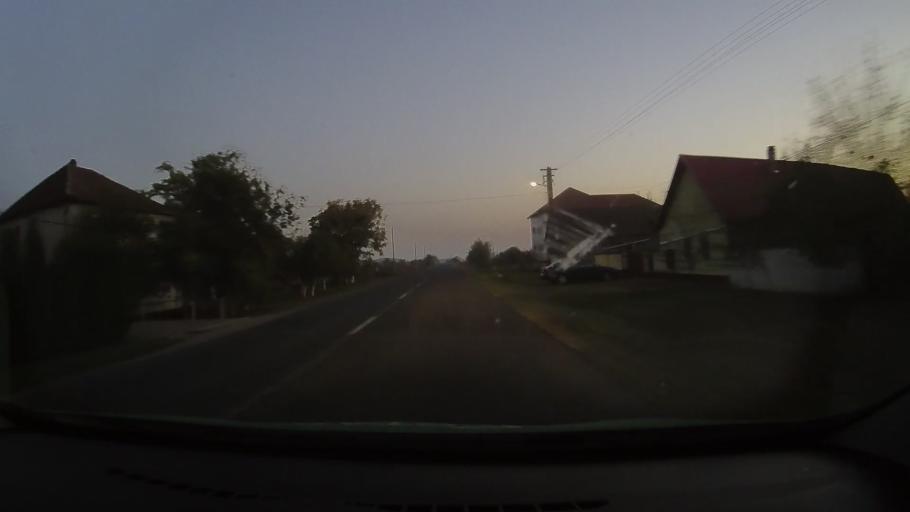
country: RO
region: Arad
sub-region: Comuna Livada
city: Livada
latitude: 46.2092
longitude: 21.3869
